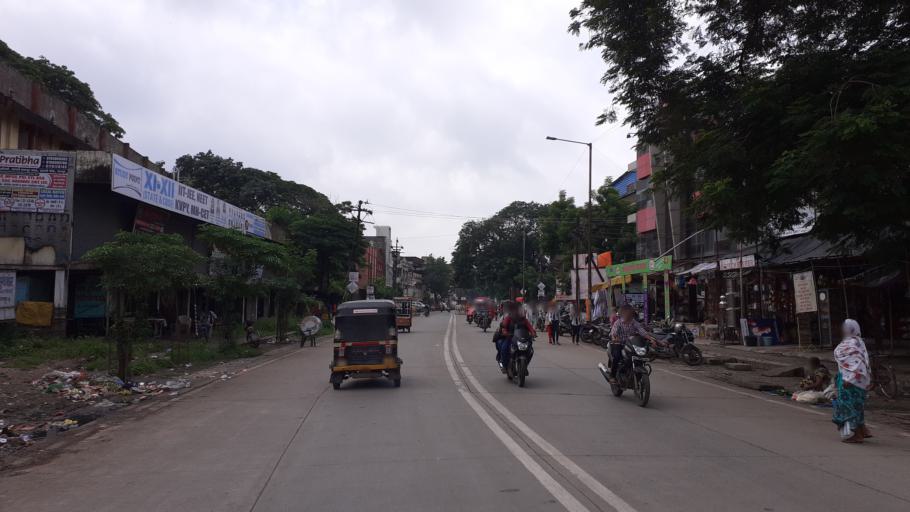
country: IN
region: Maharashtra
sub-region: Nagpur Division
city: Nagpur
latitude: 21.1260
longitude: 79.1131
